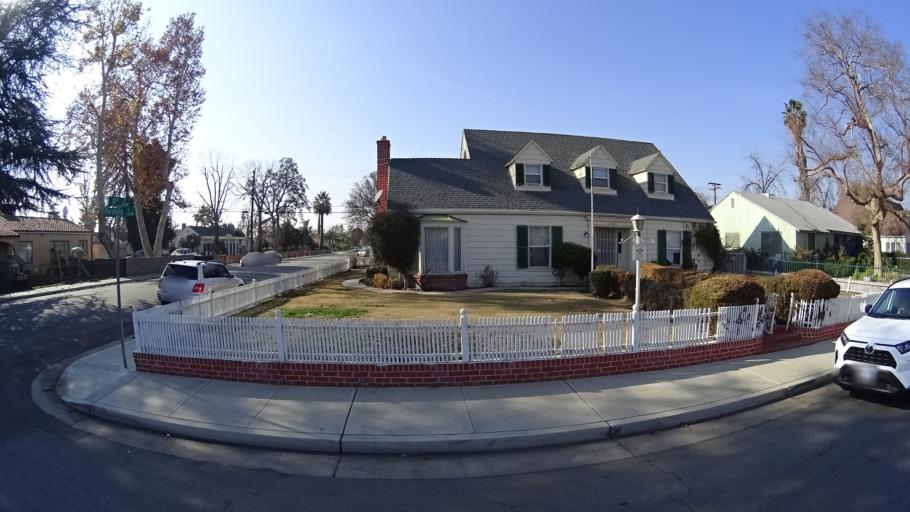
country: US
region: California
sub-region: Kern County
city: Bakersfield
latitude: 35.3675
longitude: -119.0042
